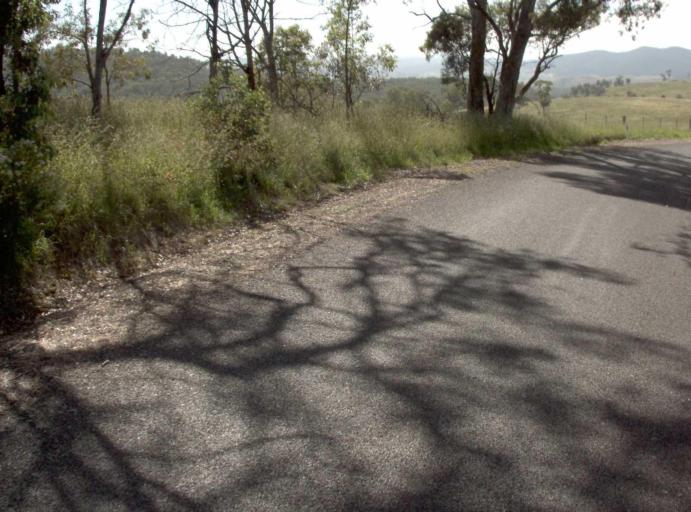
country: AU
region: Victoria
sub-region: East Gippsland
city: Lakes Entrance
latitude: -37.4877
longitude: 148.1294
